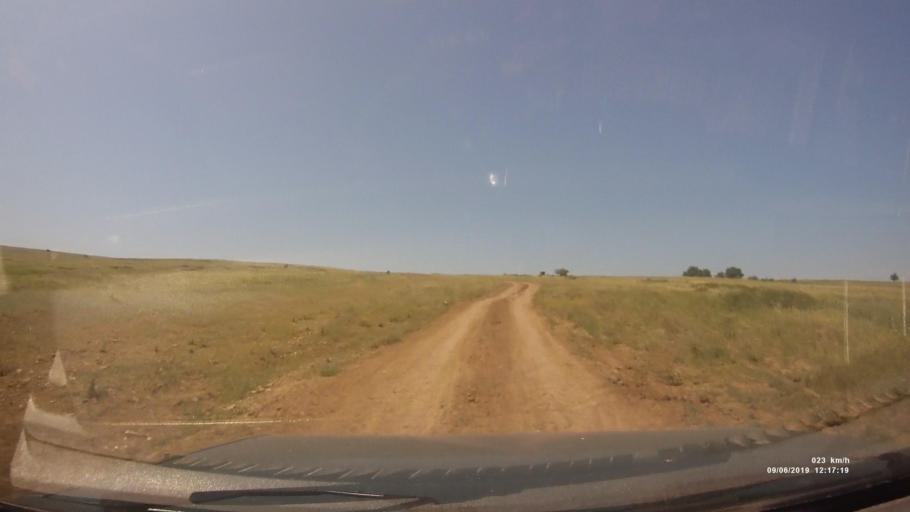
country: RU
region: Rostov
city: Staraya Stanitsa
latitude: 48.2554
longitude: 40.3161
